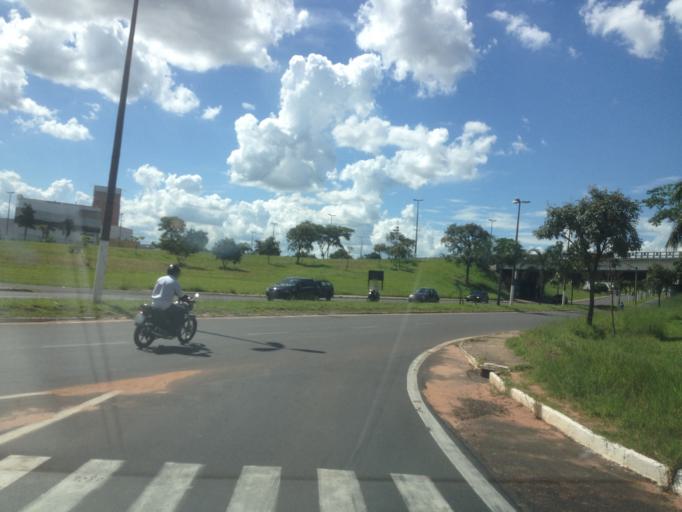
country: BR
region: Sao Paulo
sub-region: Marilia
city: Marilia
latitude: -22.2333
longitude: -49.9293
